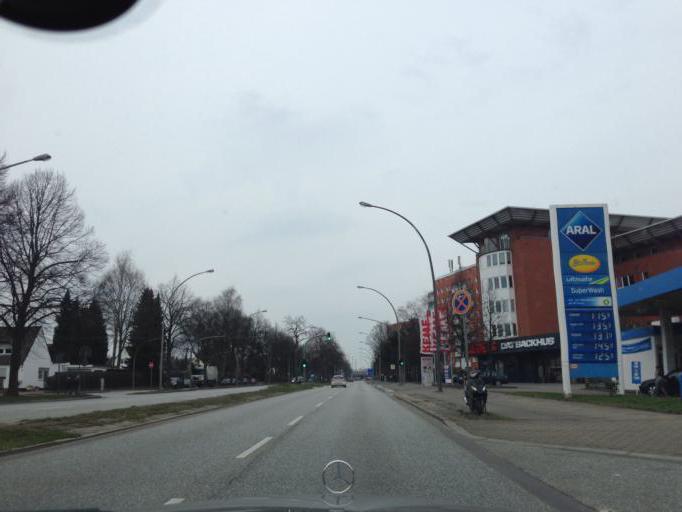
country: DE
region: Hamburg
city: Wandsbek
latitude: 53.5620
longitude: 10.1196
